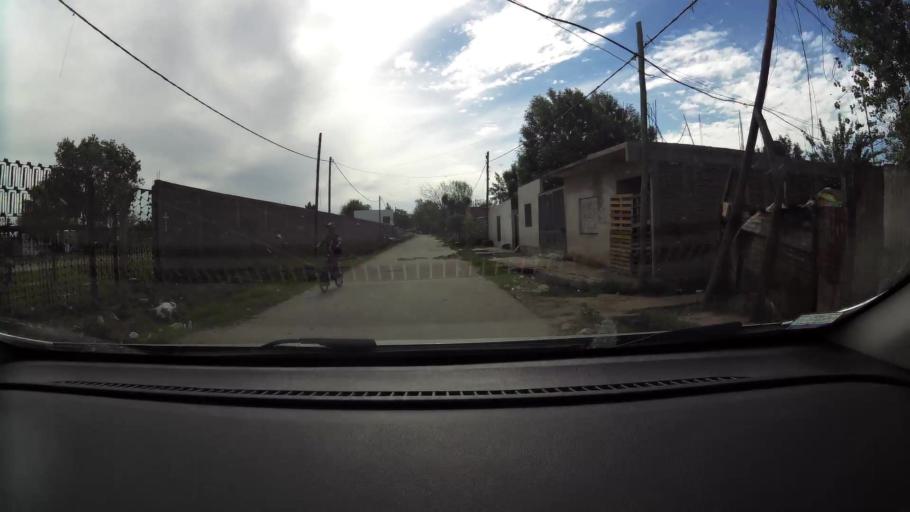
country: AR
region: Santa Fe
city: Granadero Baigorria
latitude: -32.9110
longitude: -60.7034
